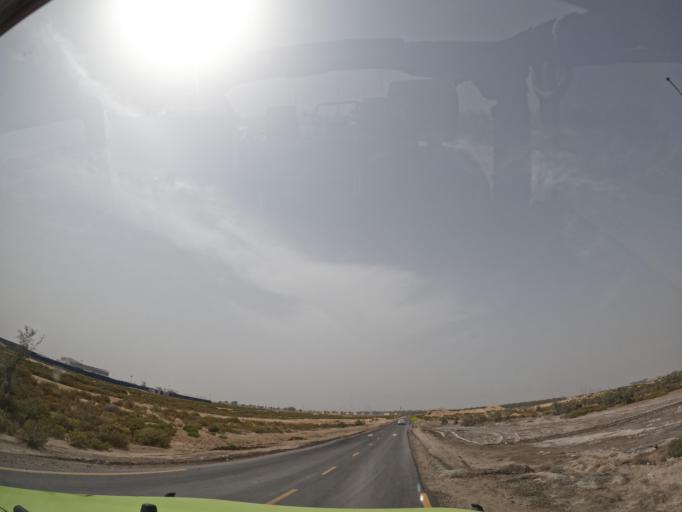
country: AE
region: Dubai
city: Dubai
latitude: 25.1249
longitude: 55.3437
